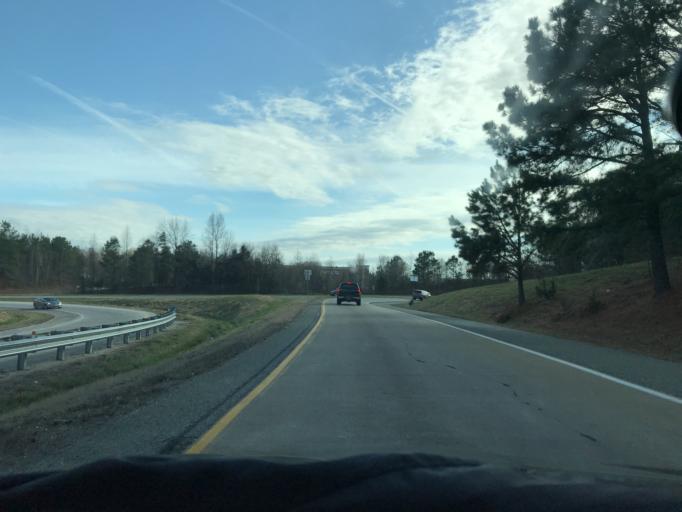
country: US
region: Virginia
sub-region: Chesterfield County
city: Brandermill
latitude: 37.4245
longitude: -77.6323
